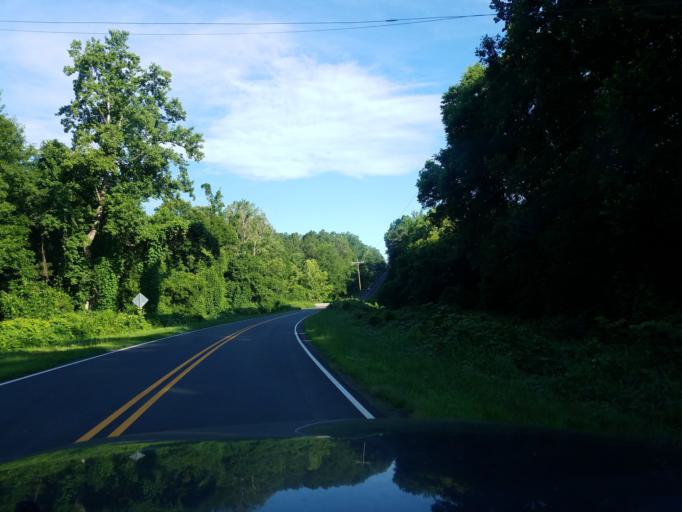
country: US
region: North Carolina
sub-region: Granville County
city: Butner
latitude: 36.1570
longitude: -78.7730
